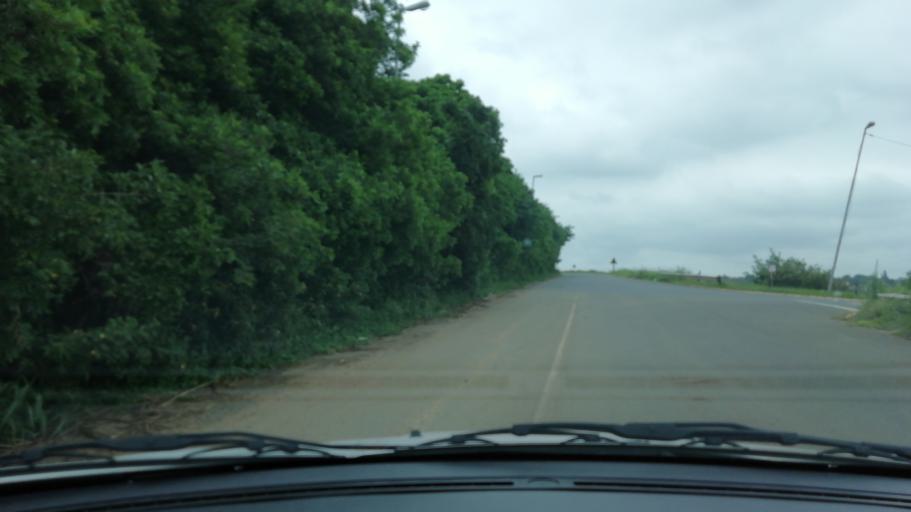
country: ZA
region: KwaZulu-Natal
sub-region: uThungulu District Municipality
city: Empangeni
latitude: -28.7380
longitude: 31.9071
